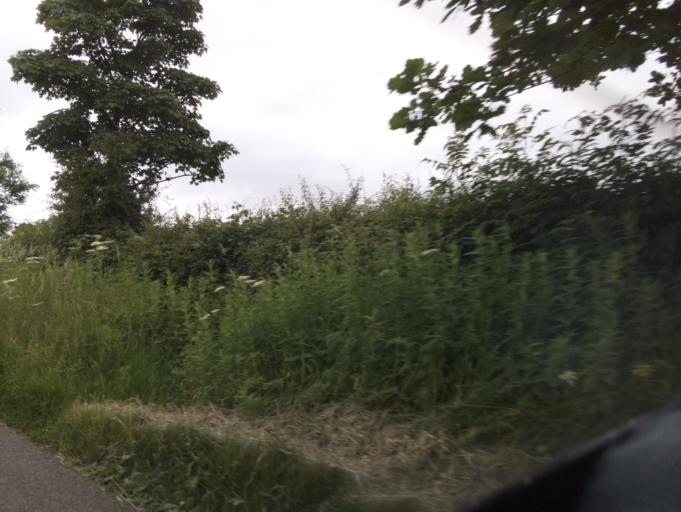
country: GB
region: England
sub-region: District of Rutland
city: Langham
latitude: 52.6813
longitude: -0.8227
